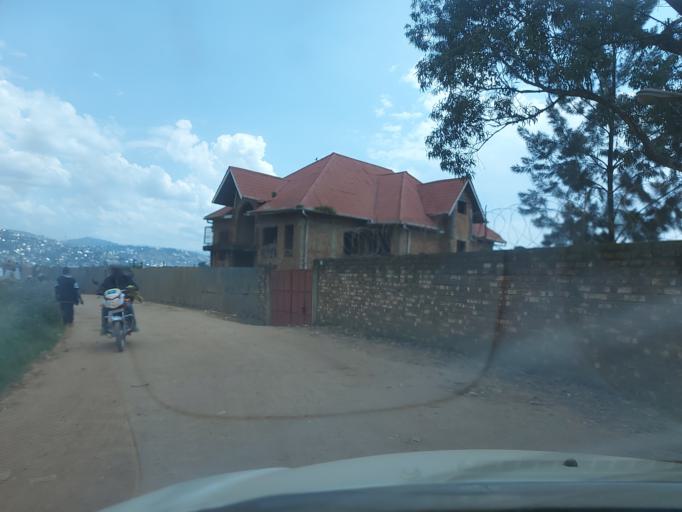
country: CD
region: South Kivu
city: Bukavu
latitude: -2.4945
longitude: 28.8625
